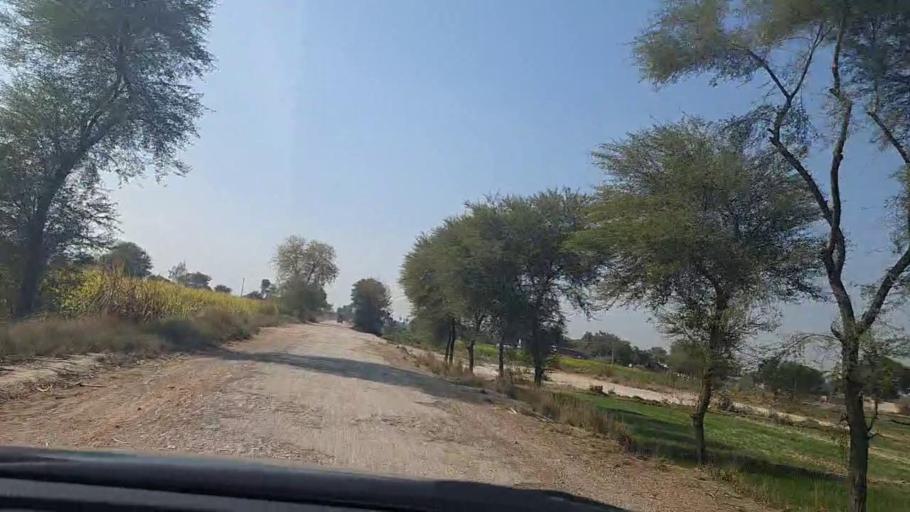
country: PK
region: Sindh
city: Daulatpur
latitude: 26.2846
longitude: 68.0512
